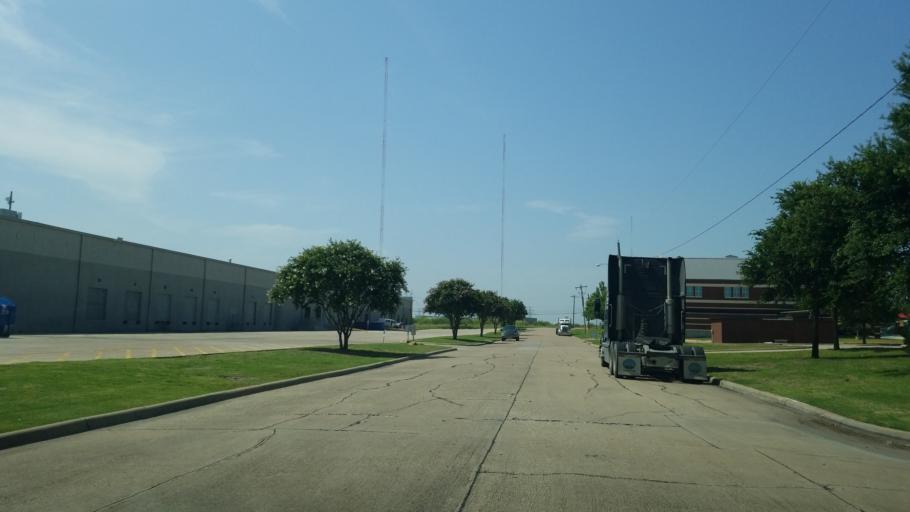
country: US
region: Texas
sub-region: Dallas County
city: Coppell
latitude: 32.9501
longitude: -96.9908
